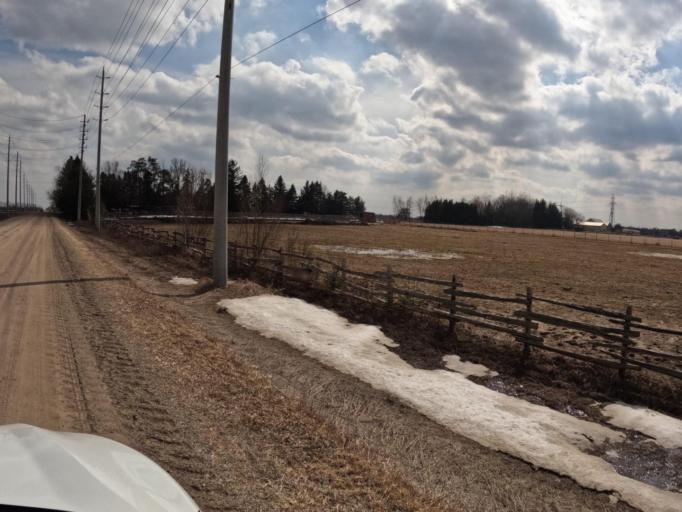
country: CA
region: Ontario
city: Shelburne
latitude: 43.9643
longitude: -80.3000
